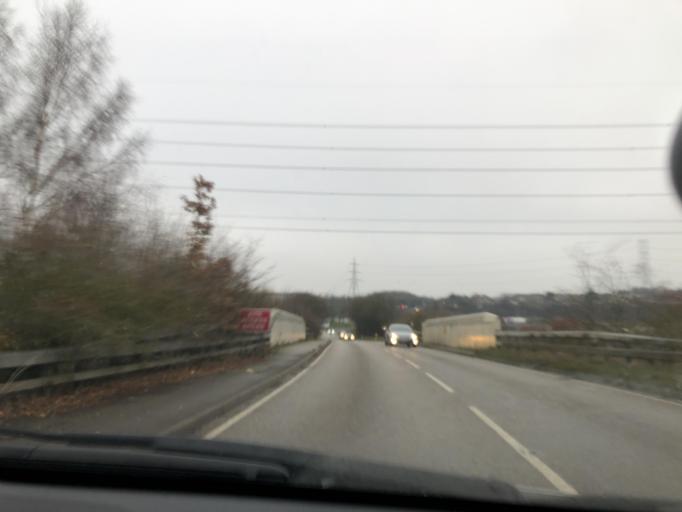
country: GB
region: England
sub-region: Kent
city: Swanscombe
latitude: 51.4230
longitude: 0.3284
